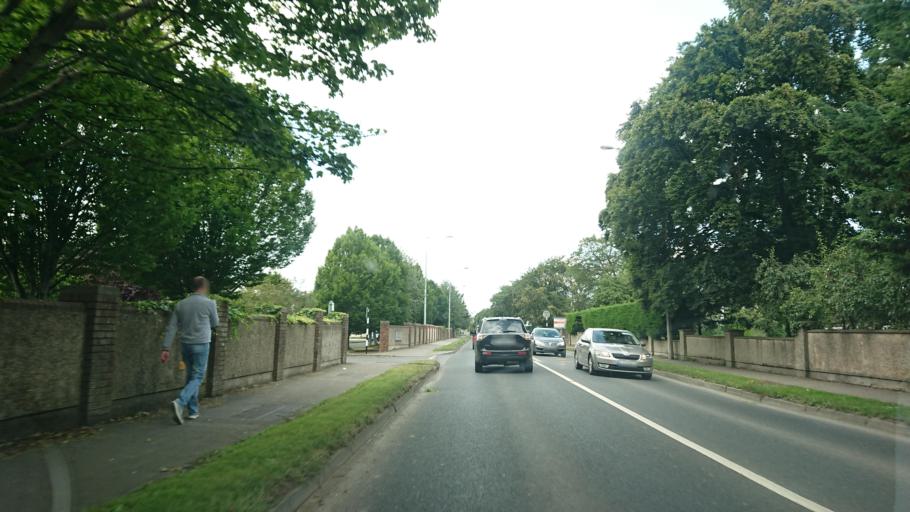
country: IE
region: Leinster
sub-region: Kildare
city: Sallins
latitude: 53.2370
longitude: -6.6520
